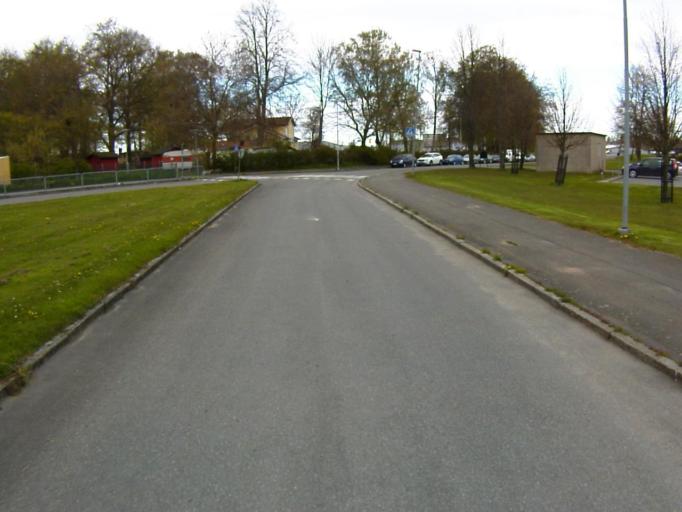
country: SE
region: Skane
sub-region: Kristianstads Kommun
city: Kristianstad
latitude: 56.0189
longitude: 14.1283
